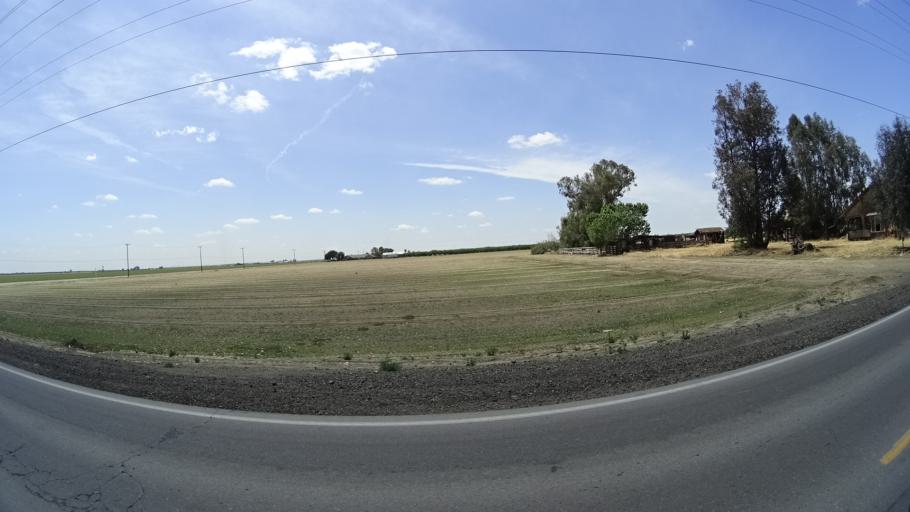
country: US
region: California
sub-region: Kings County
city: Home Garden
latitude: 36.2984
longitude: -119.6203
